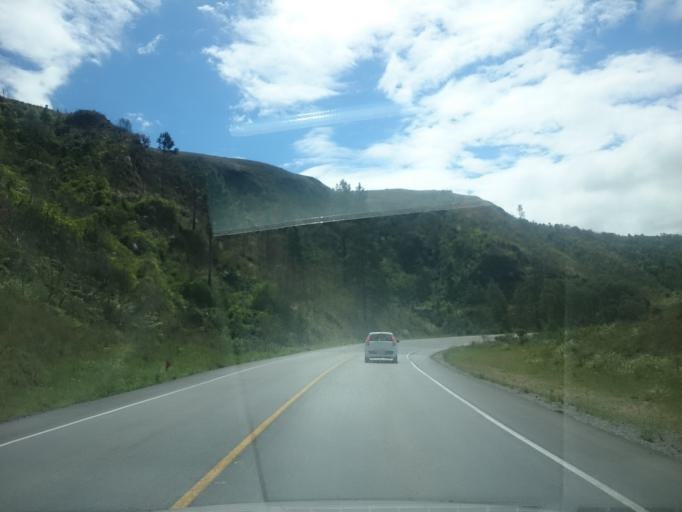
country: BR
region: Santa Catarina
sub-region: Anitapolis
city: Anitapolis
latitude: -27.6671
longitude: -49.1599
